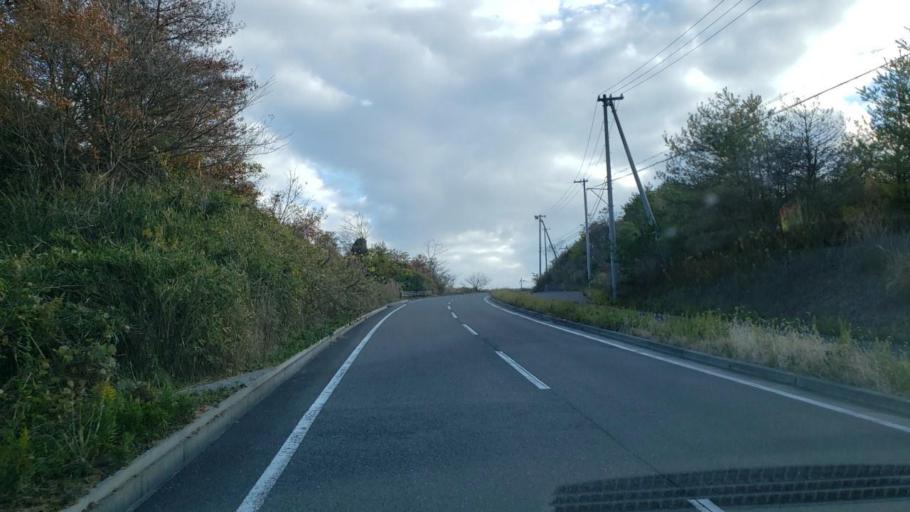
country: JP
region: Hyogo
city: Akashi
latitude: 34.5660
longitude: 134.9762
